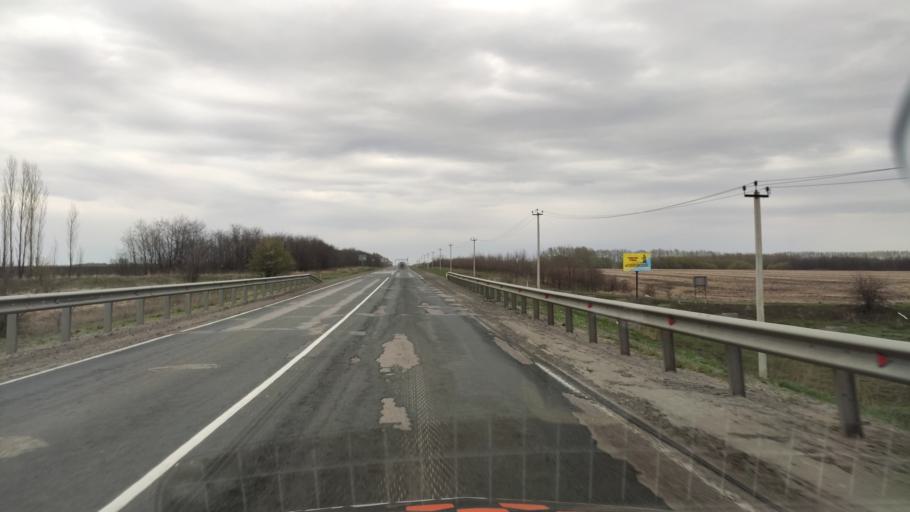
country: RU
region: Voronezj
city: Nizhnedevitsk
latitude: 51.5648
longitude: 38.2649
